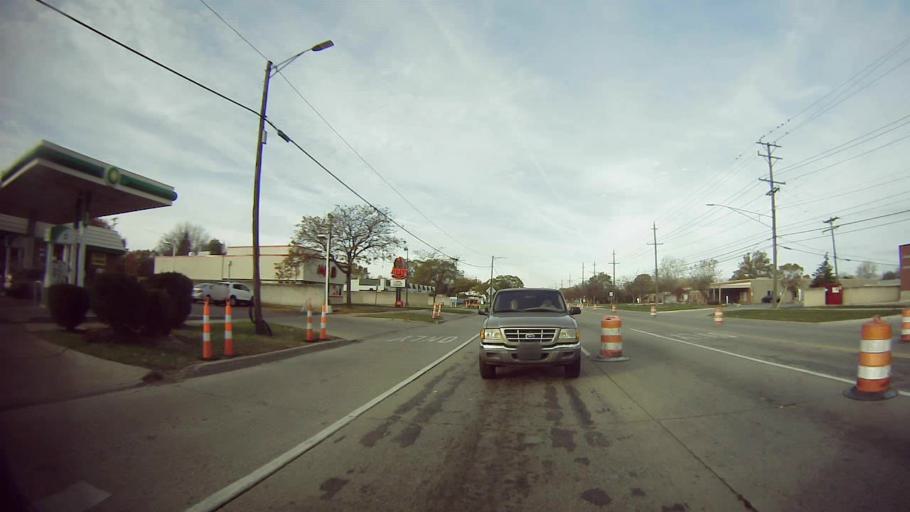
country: US
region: Michigan
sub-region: Macomb County
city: Warren
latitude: 42.4778
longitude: -83.0066
